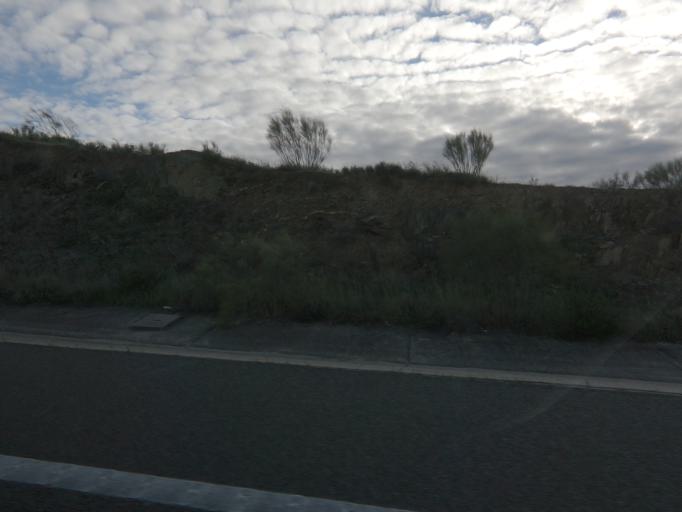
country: ES
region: Extremadura
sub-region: Provincia de Caceres
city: Hinojal
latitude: 39.7079
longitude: -6.4077
